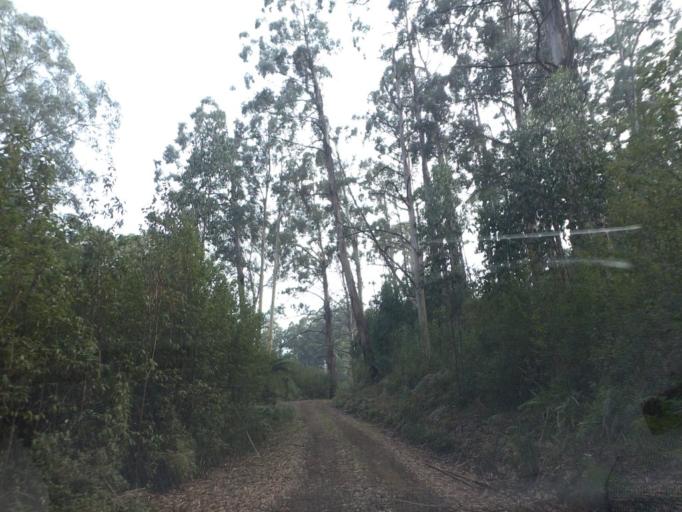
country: AU
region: Victoria
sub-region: Yarra Ranges
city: Healesville
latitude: -37.5765
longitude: 145.5203
